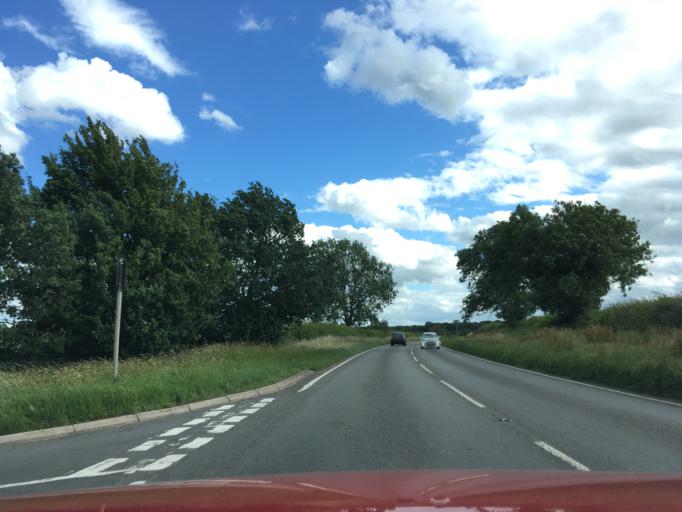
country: GB
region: England
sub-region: Leicestershire
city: Donisthorpe
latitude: 52.6837
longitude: -1.5454
